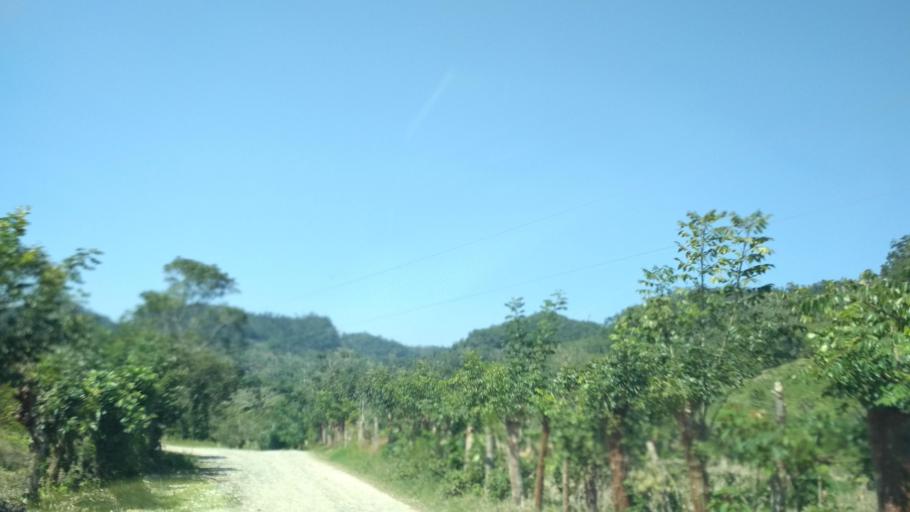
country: MX
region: Veracruz
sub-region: Papantla
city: Polutla
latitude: 20.4793
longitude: -97.2215
